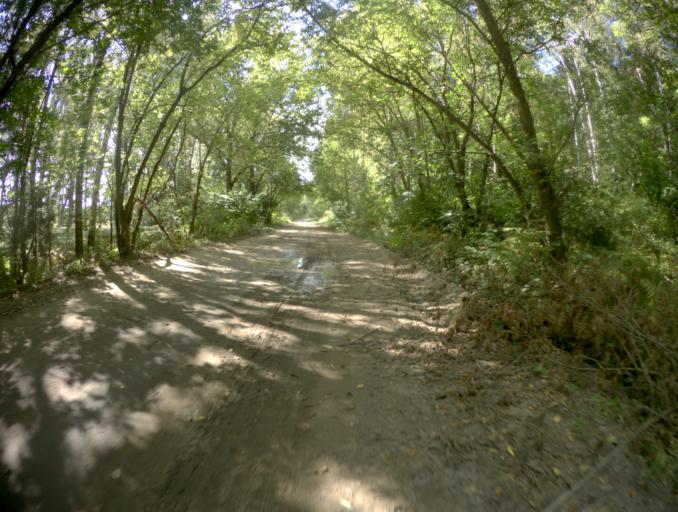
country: RU
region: Vladimir
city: Krasnaya Gorbatka
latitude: 55.8604
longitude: 41.8042
